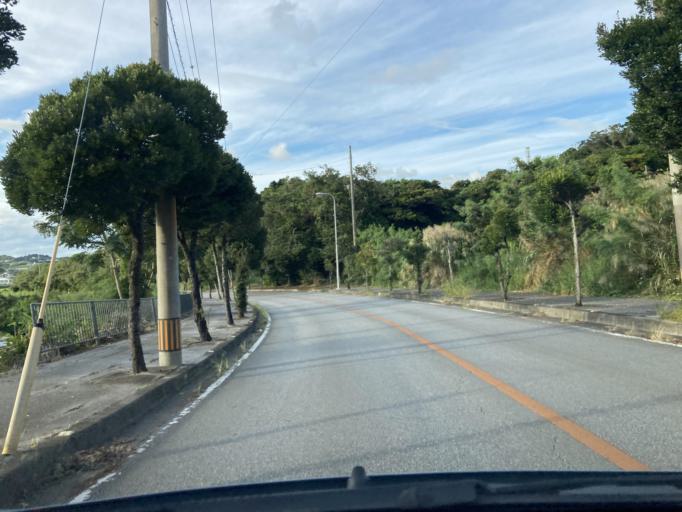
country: JP
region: Okinawa
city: Itoman
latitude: 26.1336
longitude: 127.7226
